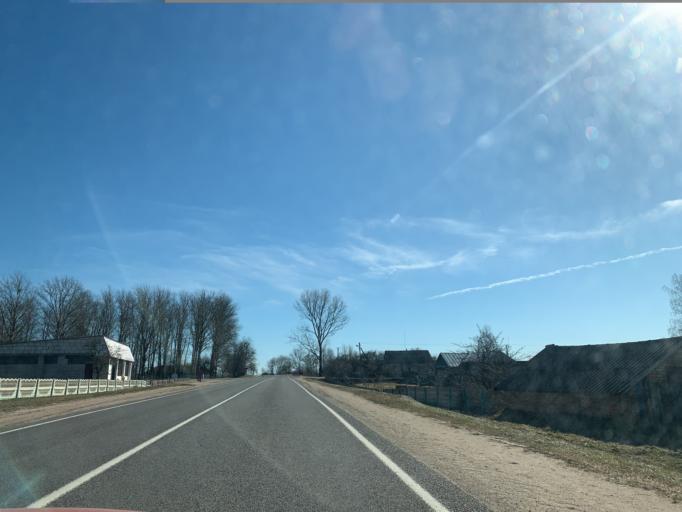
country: BY
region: Minsk
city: Nyasvizh
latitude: 53.2274
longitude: 26.7516
